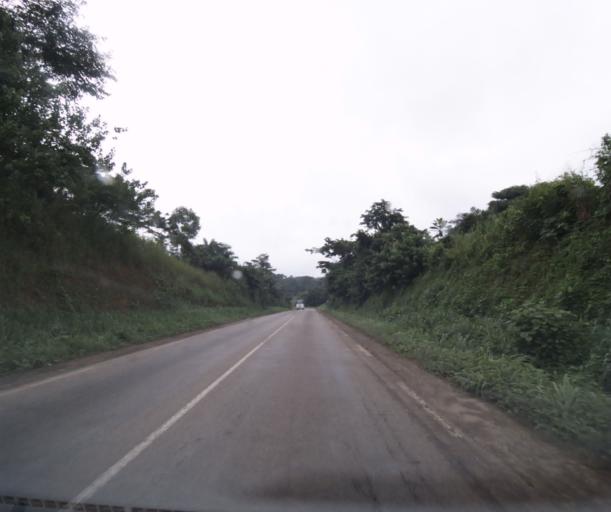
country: CM
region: Littoral
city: Edea
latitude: 3.8454
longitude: 10.4733
